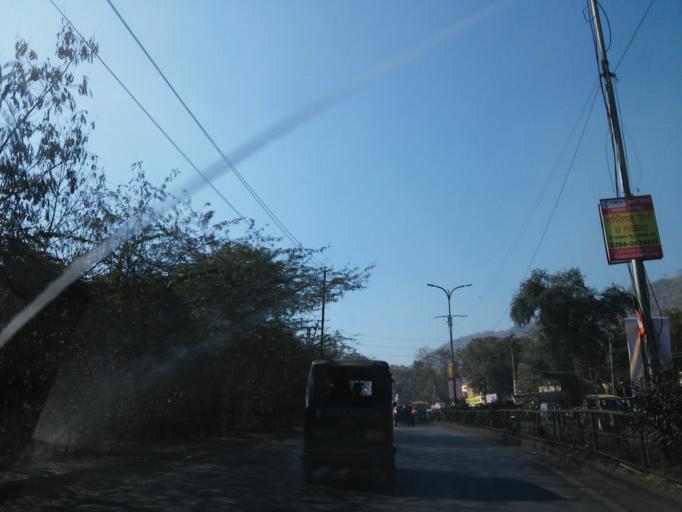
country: IN
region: Rajasthan
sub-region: Udaipur
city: Udaipur
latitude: 24.5647
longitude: 73.6938
